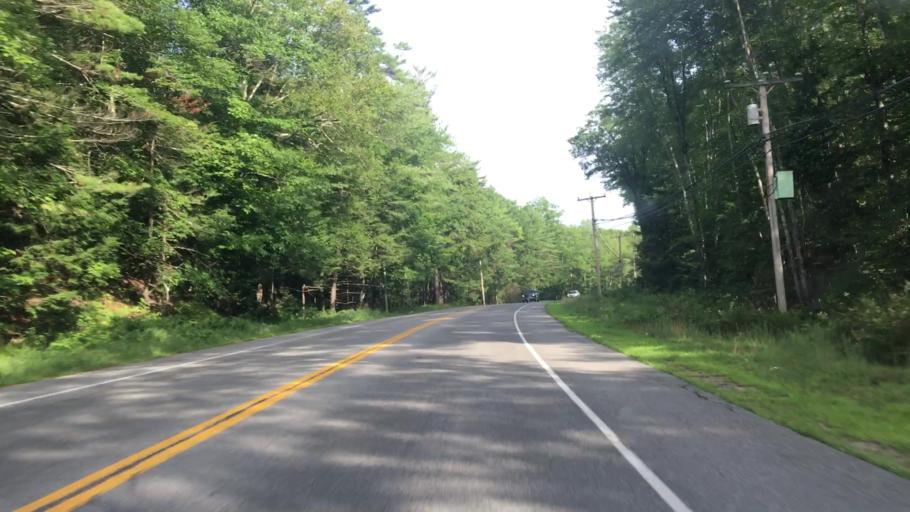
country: US
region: Maine
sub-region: York County
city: Limington
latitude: 43.7392
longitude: -70.6725
